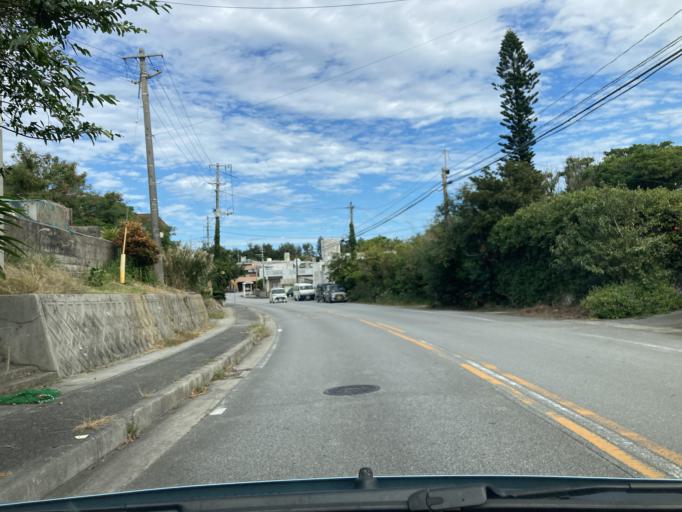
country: JP
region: Okinawa
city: Ishikawa
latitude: 26.4359
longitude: 127.7781
